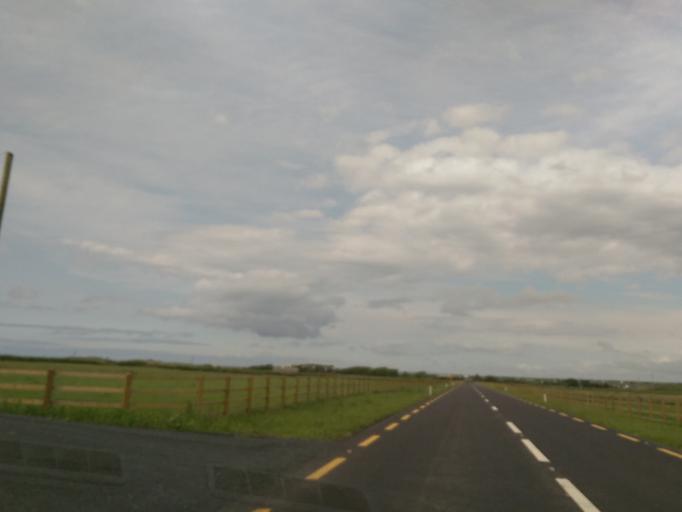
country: IE
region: Munster
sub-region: An Clar
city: Kilrush
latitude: 52.7401
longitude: -9.4817
